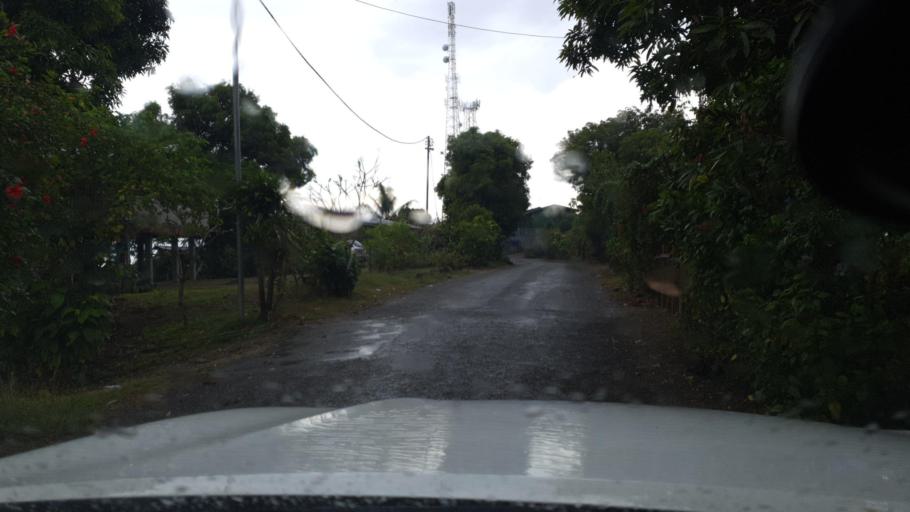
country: SB
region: Guadalcanal
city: Honiara
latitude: -9.4409
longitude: 159.9495
